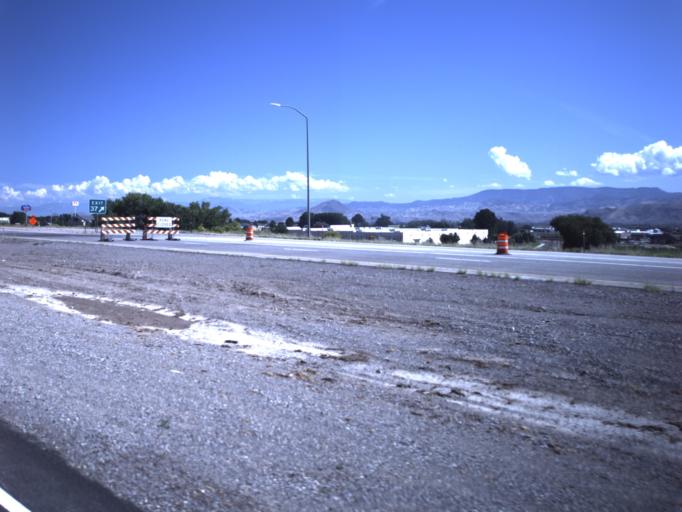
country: US
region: Utah
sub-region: Sevier County
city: Richfield
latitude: 38.7456
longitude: -112.1084
